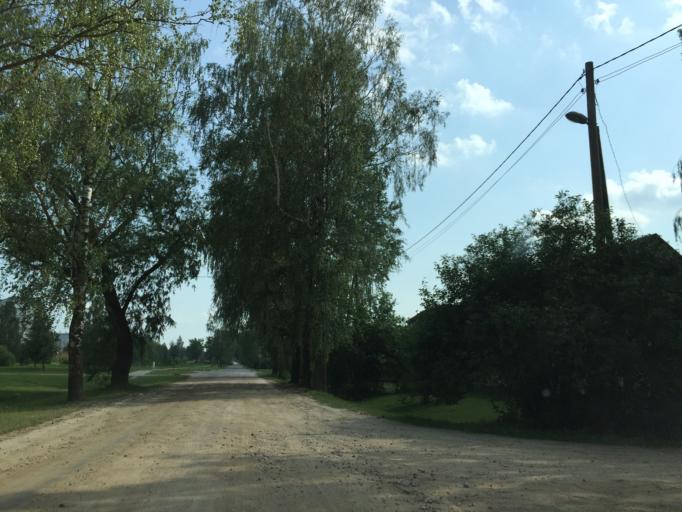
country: LV
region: Jelgava
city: Jelgava
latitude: 56.6715
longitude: 23.7422
